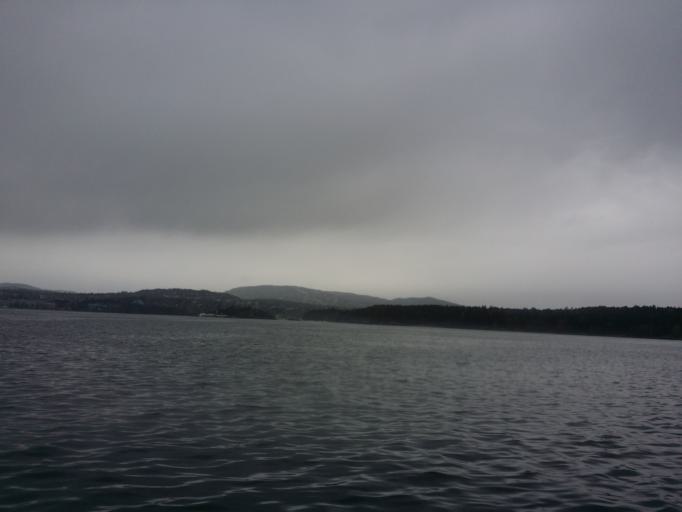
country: NO
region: Akershus
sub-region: Nesodden
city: Nesoddtangen
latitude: 59.8924
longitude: 10.6610
